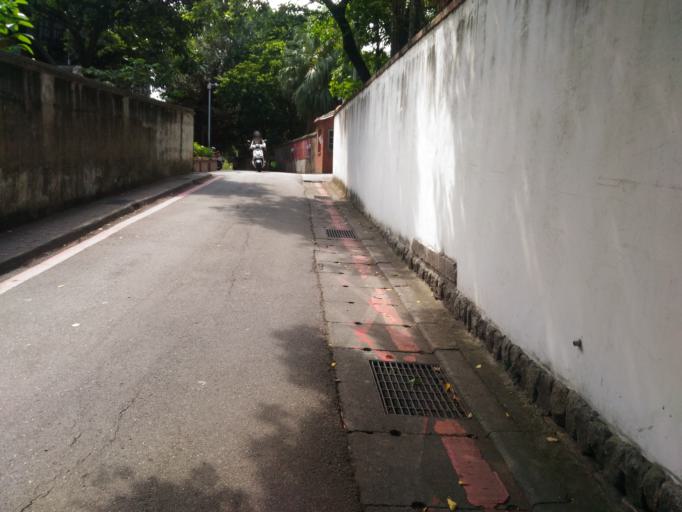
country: TW
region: Taipei
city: Taipei
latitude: 25.1750
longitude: 121.4356
